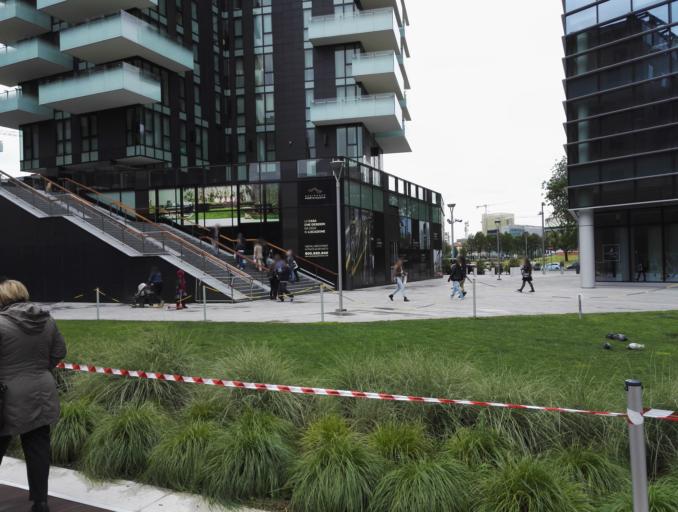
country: IT
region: Lombardy
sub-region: Citta metropolitana di Milano
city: Milano
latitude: 45.4816
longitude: 9.1942
